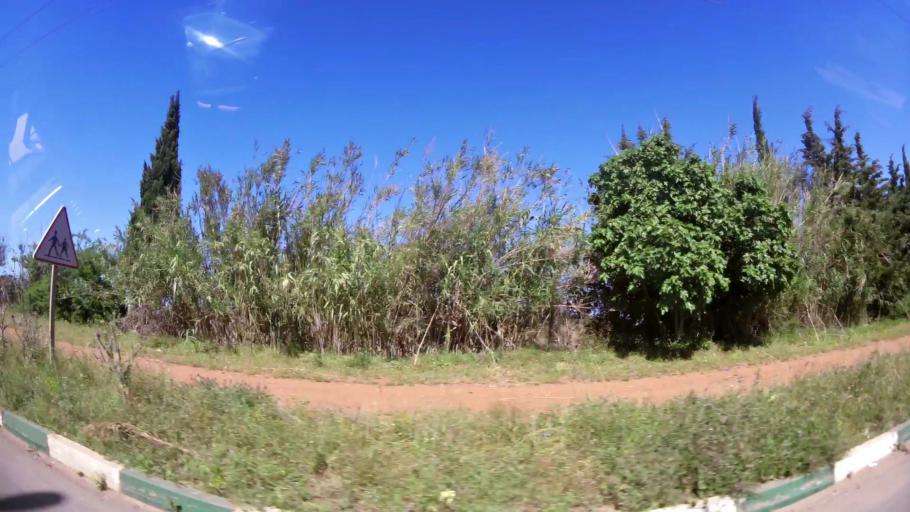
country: MA
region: Oriental
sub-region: Berkane-Taourirt
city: Berkane
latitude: 34.9432
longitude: -2.3258
